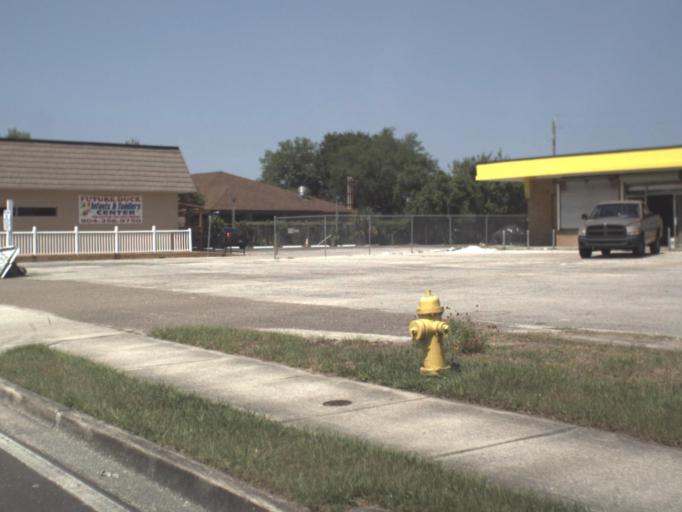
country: US
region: Florida
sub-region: Duval County
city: Jacksonville
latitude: 30.3663
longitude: -81.6632
